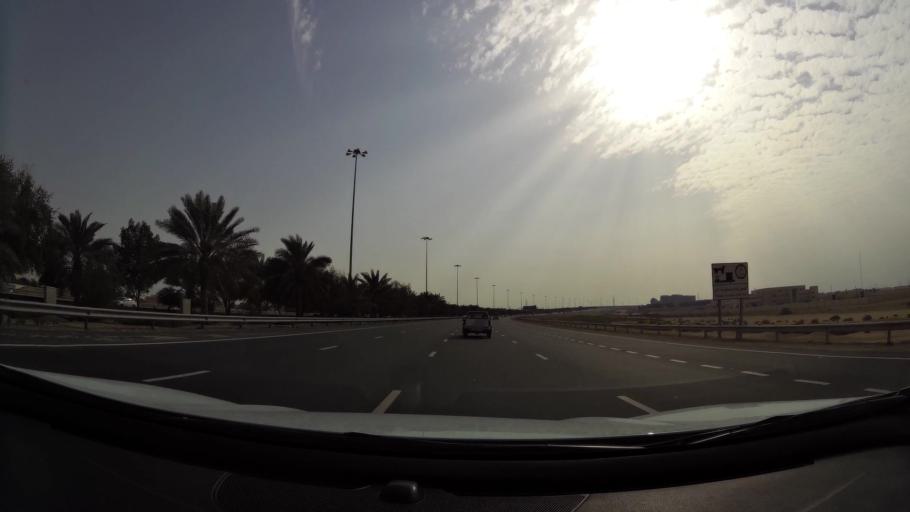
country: AE
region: Abu Dhabi
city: Abu Dhabi
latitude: 24.3359
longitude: 54.6337
